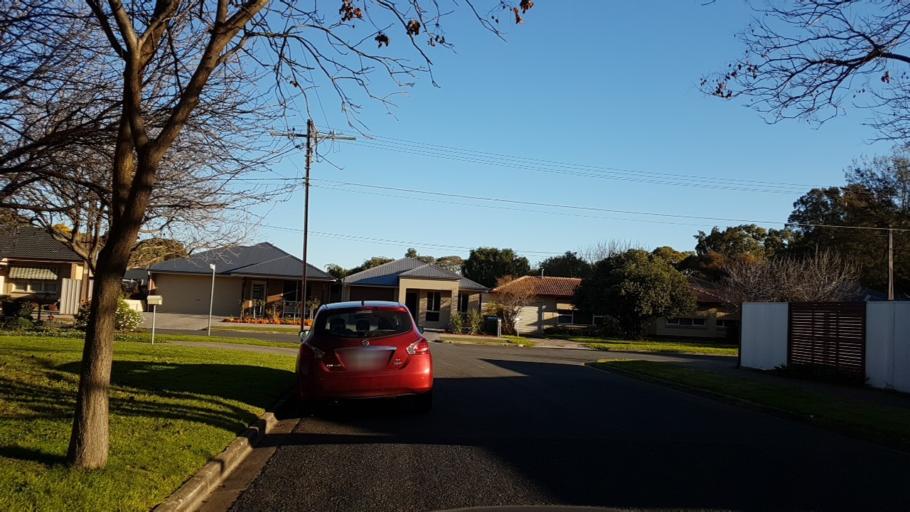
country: AU
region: South Australia
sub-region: Campbelltown
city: Hectorville
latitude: -34.8799
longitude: 138.6532
